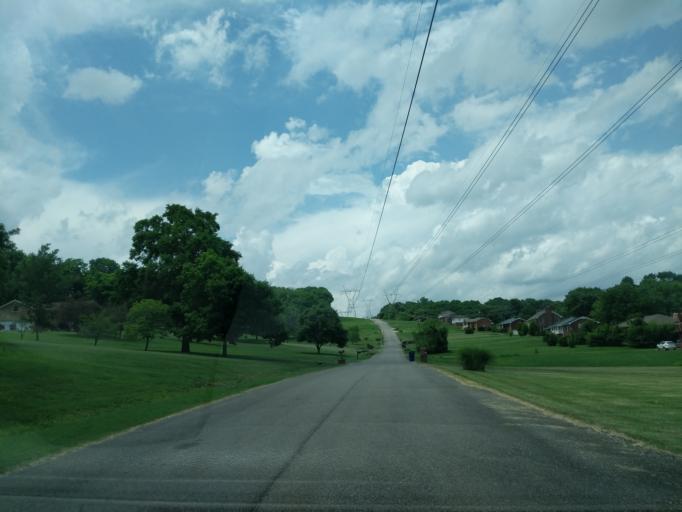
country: US
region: Tennessee
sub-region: Davidson County
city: Goodlettsville
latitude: 36.3066
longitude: -86.7267
